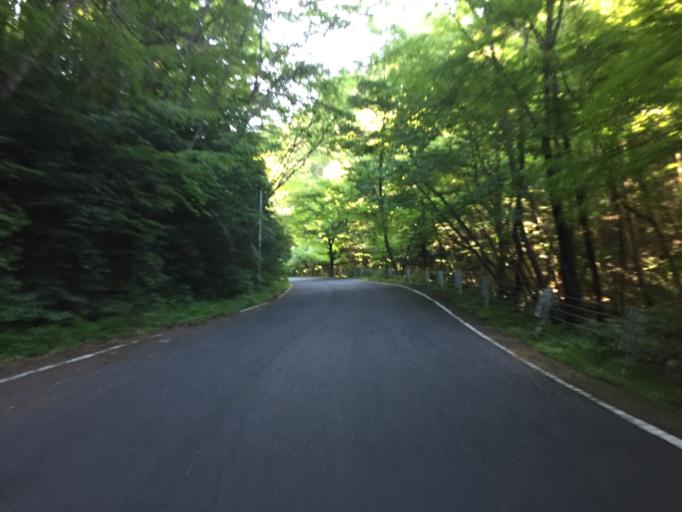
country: JP
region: Ibaraki
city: Kitaibaraki
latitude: 36.8812
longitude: 140.6321
